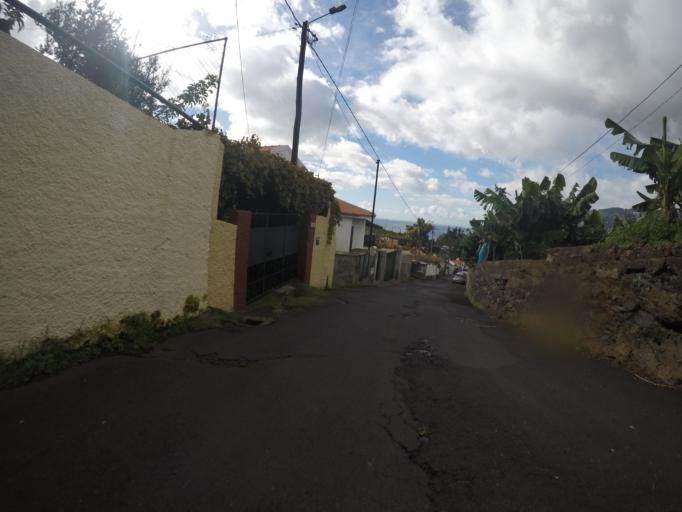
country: PT
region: Madeira
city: Camara de Lobos
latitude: 32.6496
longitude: -16.9540
